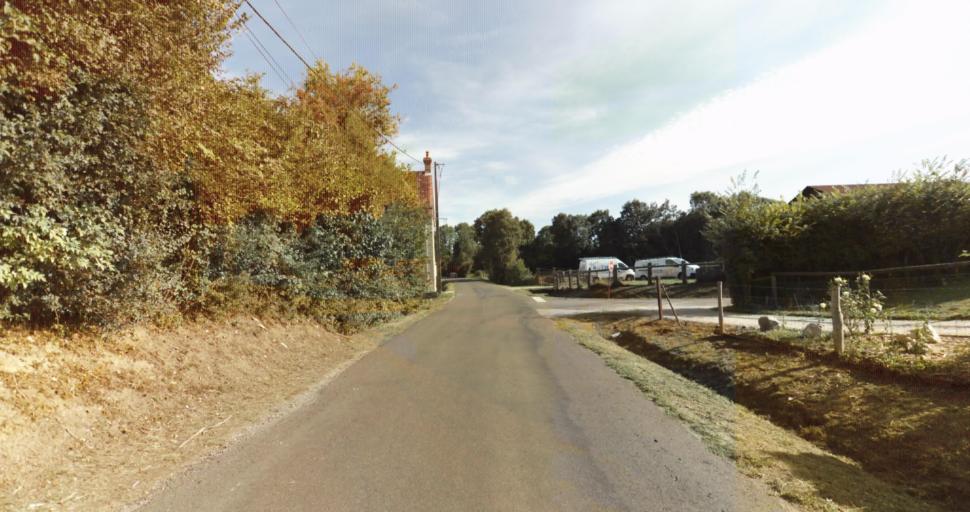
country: FR
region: Lower Normandy
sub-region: Departement de l'Orne
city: Gace
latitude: 48.7156
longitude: 0.2356
